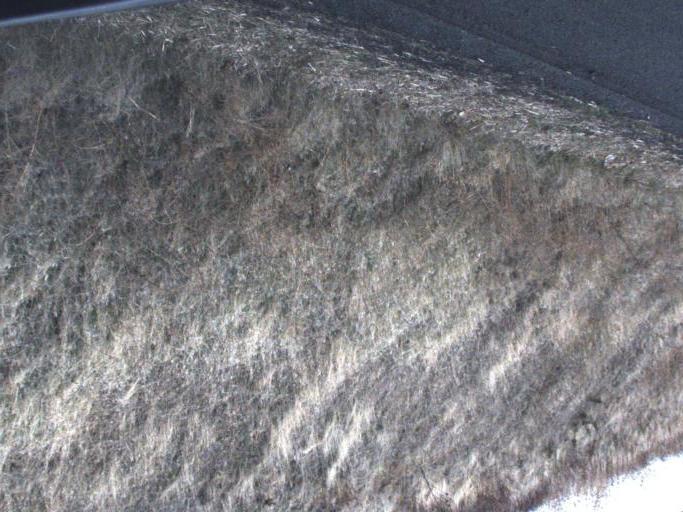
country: US
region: Washington
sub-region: Whitman County
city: Colfax
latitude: 46.8649
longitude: -117.4273
